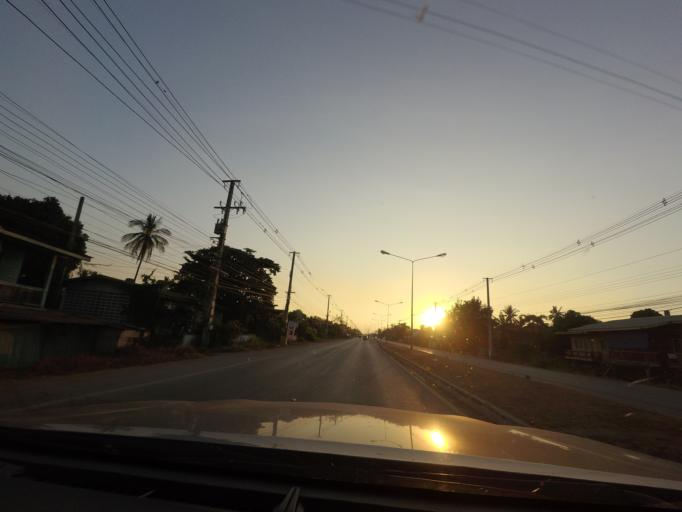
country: TH
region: Sukhothai
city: Sukhothai
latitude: 17.0582
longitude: 99.8353
